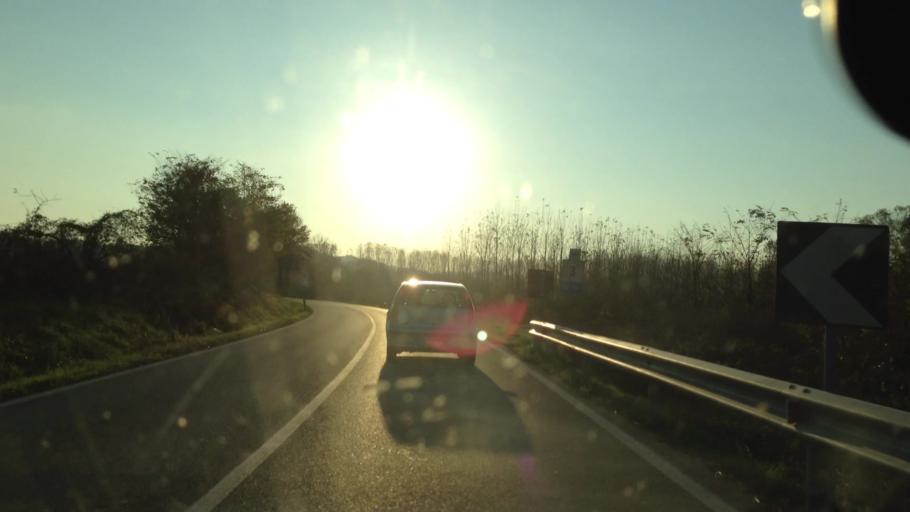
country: IT
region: Piedmont
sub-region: Provincia di Torino
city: Verrua Savoia
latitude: 45.1653
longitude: 8.0822
